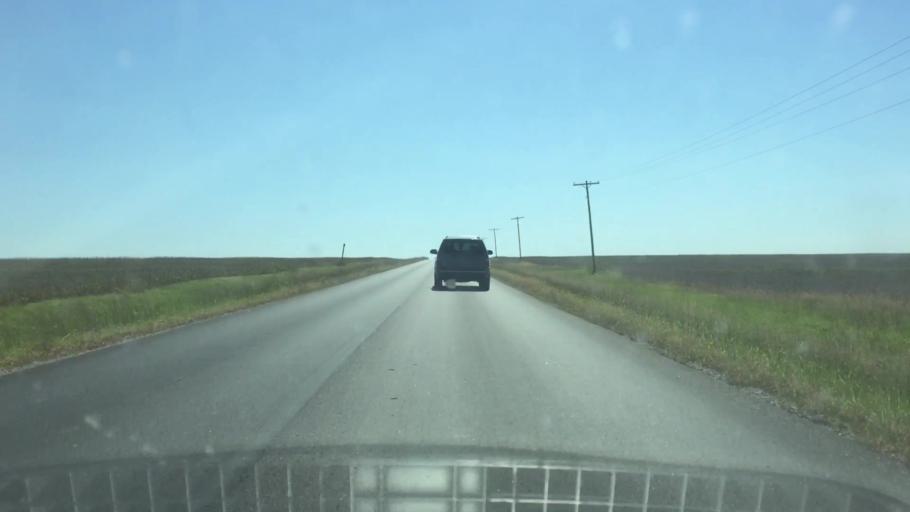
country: US
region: Kansas
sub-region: Marshall County
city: Marysville
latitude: 39.8699
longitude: -96.6009
